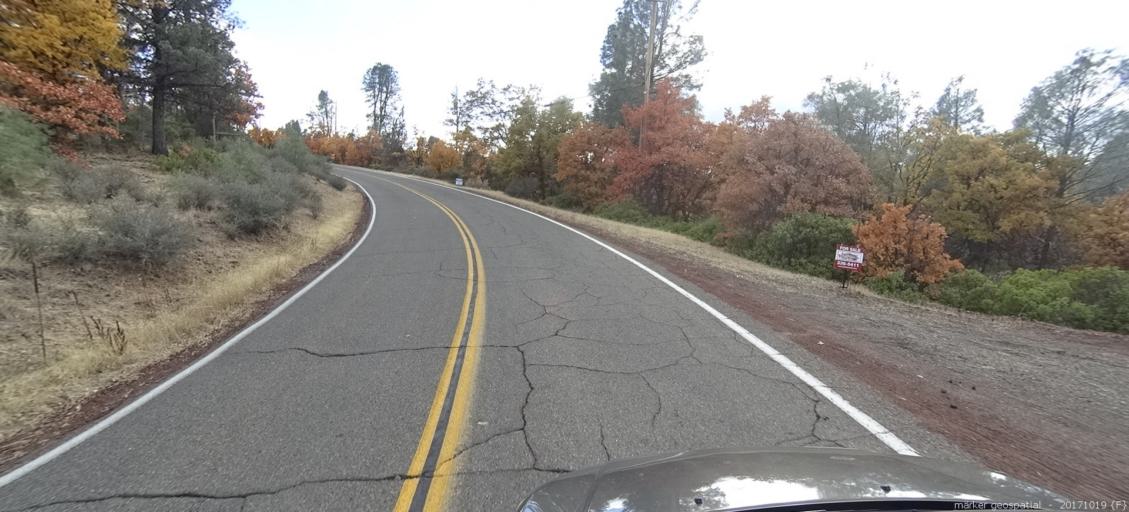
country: US
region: California
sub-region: Shasta County
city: Burney
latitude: 40.9671
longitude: -121.4352
